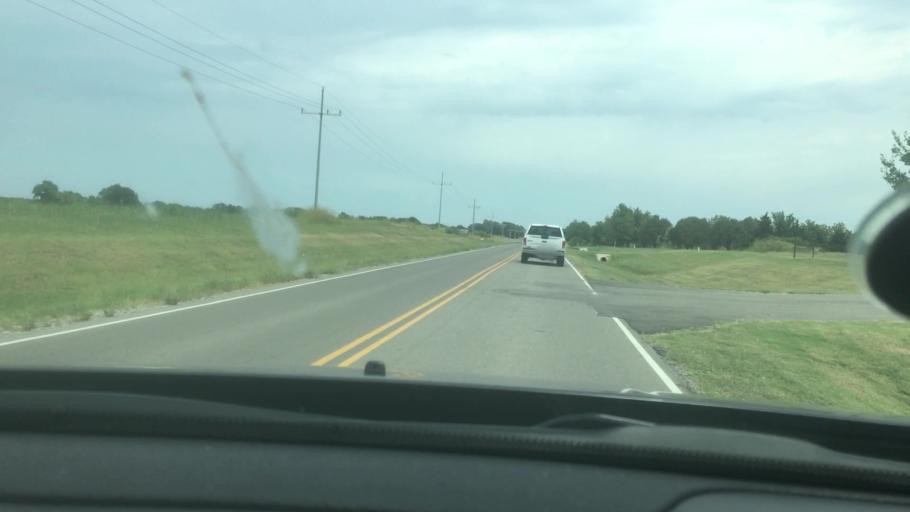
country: US
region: Oklahoma
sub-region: Murray County
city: Davis
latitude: 34.4772
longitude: -97.0663
